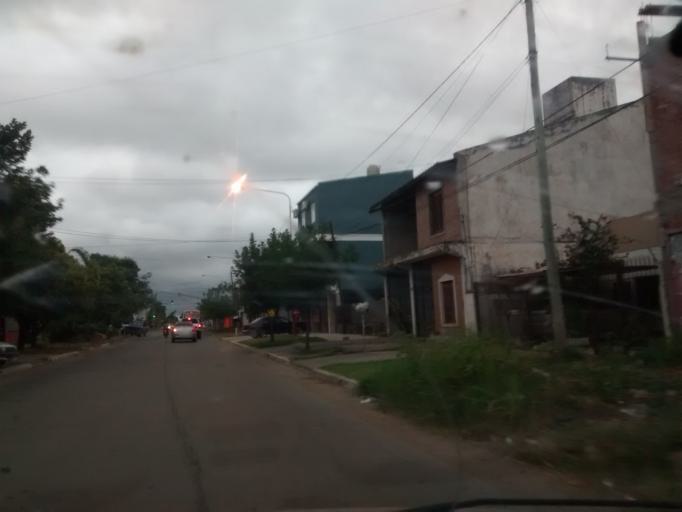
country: AR
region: Chaco
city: Resistencia
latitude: -27.4479
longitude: -59.0026
